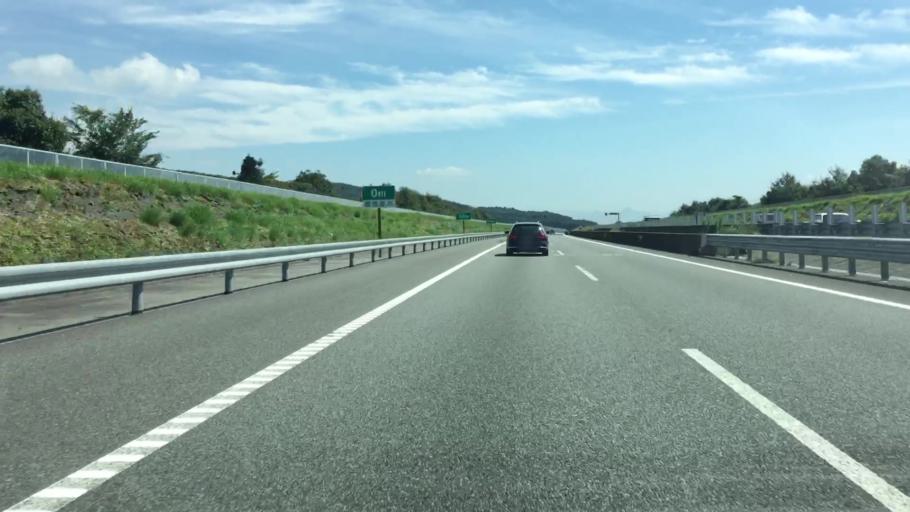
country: JP
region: Shizuoka
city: Fuji
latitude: 35.1882
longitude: 138.7199
